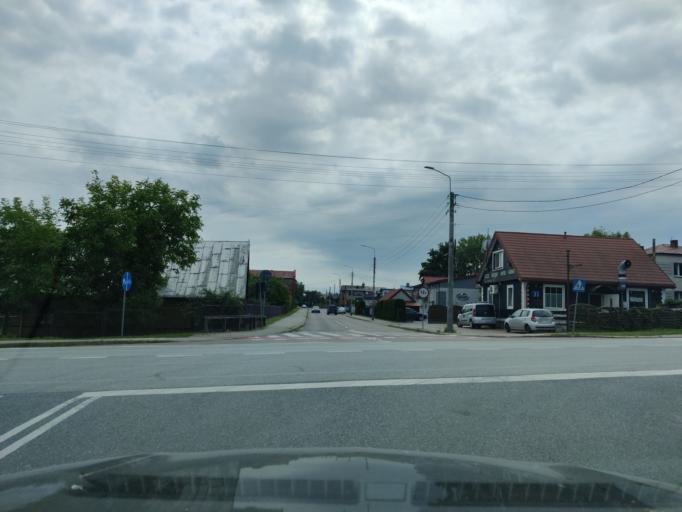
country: PL
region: Podlasie
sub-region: Powiat zambrowski
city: Zambrow
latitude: 52.9821
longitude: 22.2355
